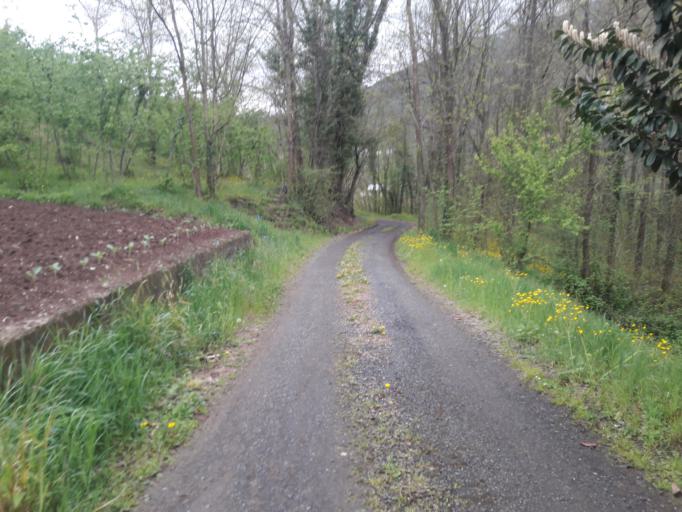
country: TR
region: Trabzon
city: Duzkoy
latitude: 40.9221
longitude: 39.4871
